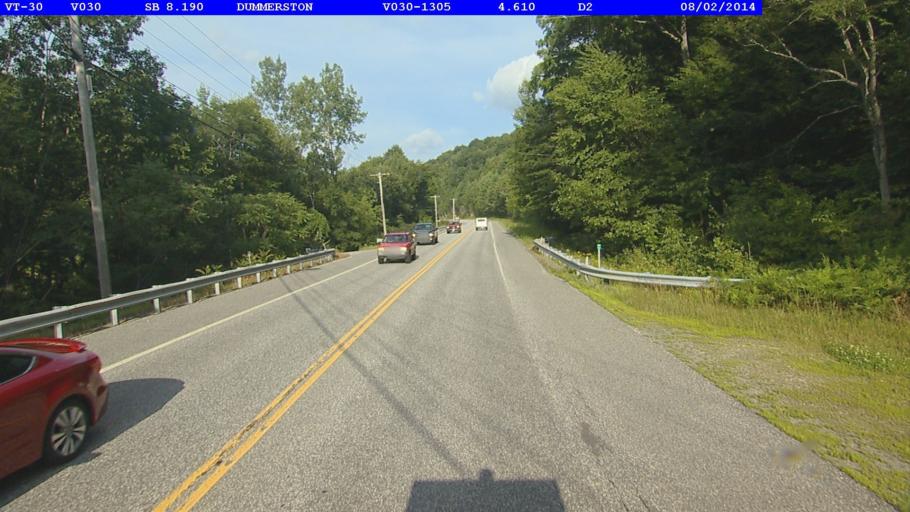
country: US
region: Vermont
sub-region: Windham County
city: Newfane
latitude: 42.9478
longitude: -72.6322
